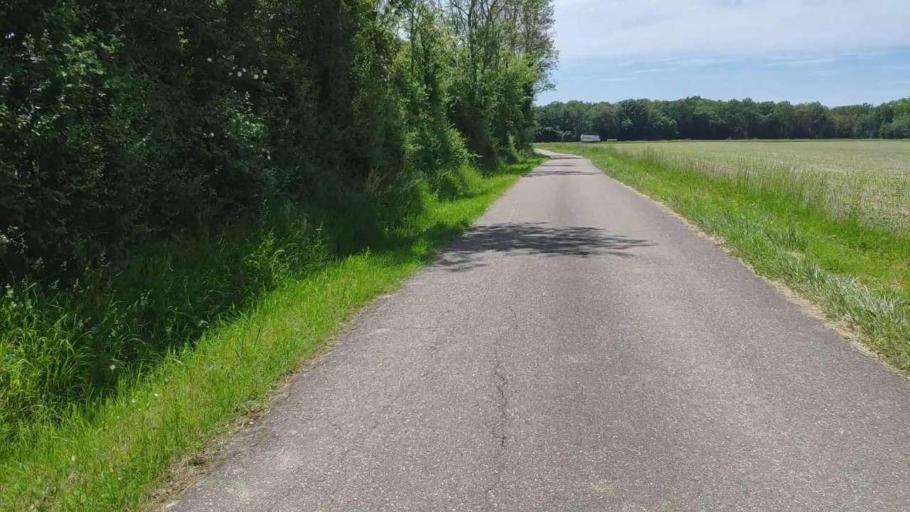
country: FR
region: Franche-Comte
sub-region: Departement du Jura
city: Bletterans
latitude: 46.7806
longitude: 5.3780
